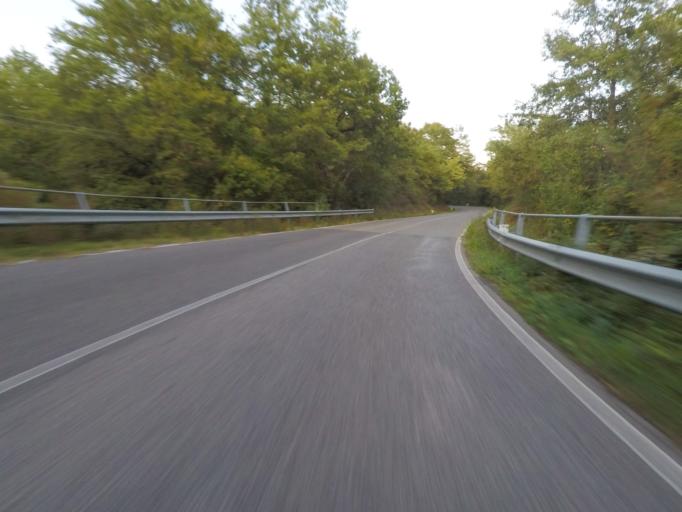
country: IT
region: Tuscany
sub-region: Provincia di Siena
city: Torrita di Siena
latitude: 43.1368
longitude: 11.7307
